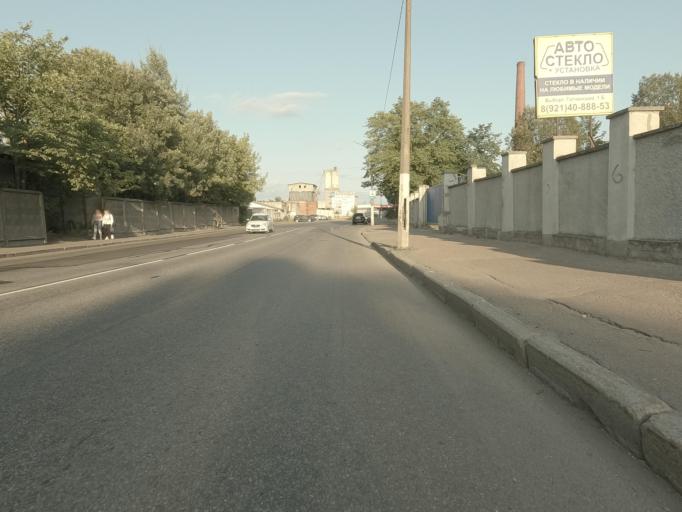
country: RU
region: Leningrad
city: Vyborg
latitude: 60.7105
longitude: 28.7683
